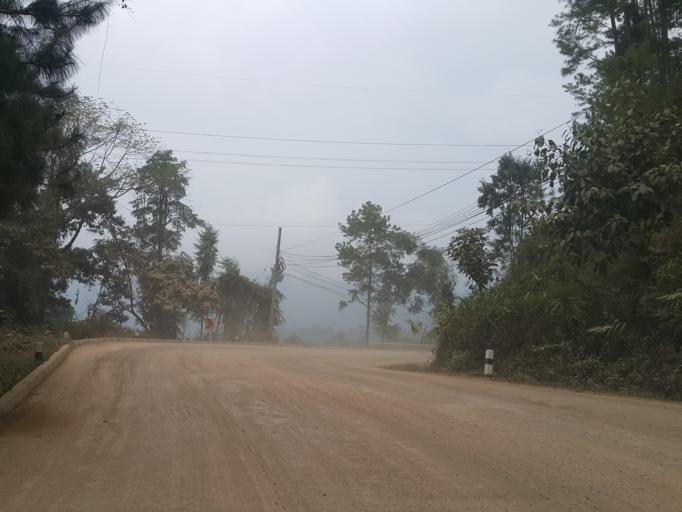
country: TH
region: Mae Hong Son
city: Mae Hi
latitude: 19.2708
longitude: 98.5450
